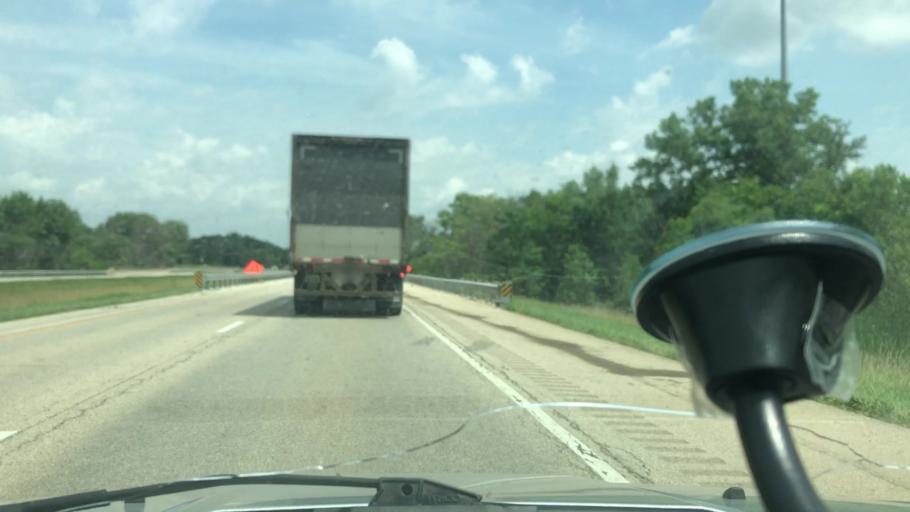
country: US
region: Illinois
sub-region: Peoria County
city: Bellevue
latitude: 40.7169
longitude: -89.6761
